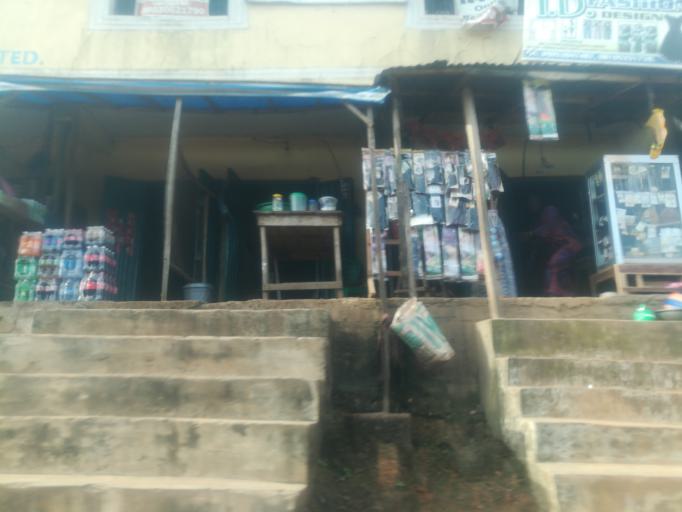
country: NG
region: Oyo
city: Ibadan
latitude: 7.3446
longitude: 3.9158
